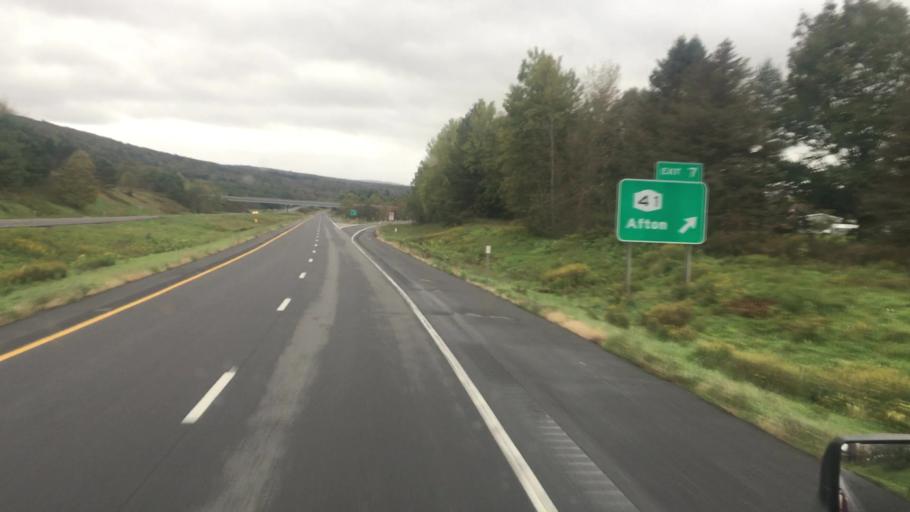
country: US
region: New York
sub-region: Chenango County
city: Bainbridge
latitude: 42.2281
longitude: -75.5114
